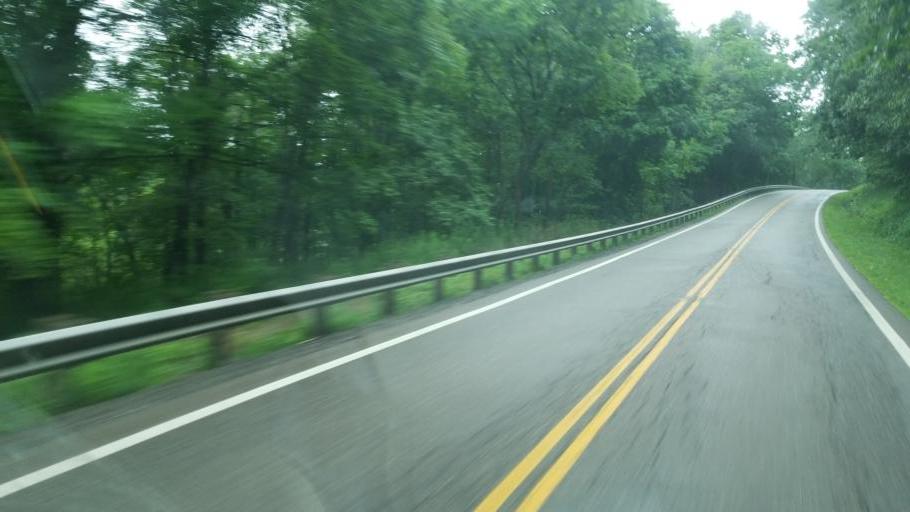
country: US
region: Ohio
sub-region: Carroll County
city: Carrollton
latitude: 40.4650
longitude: -80.9357
